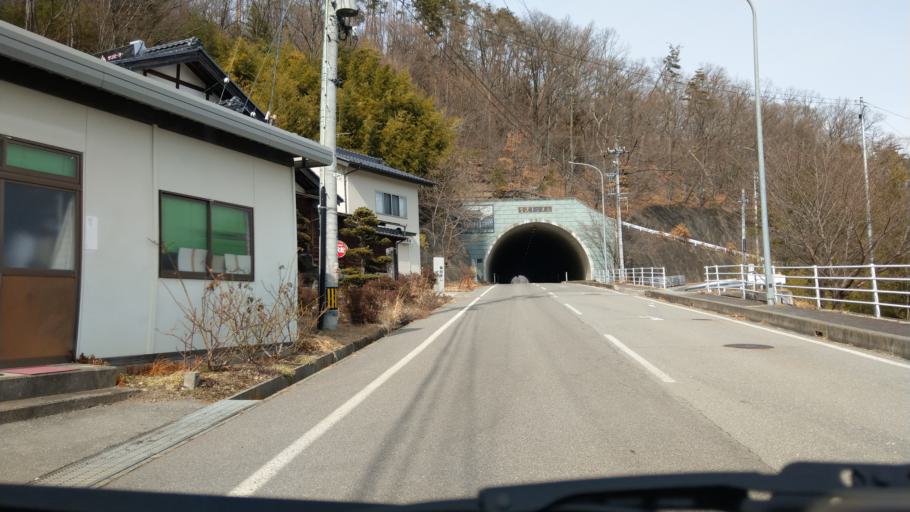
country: JP
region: Nagano
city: Komoro
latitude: 36.2948
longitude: 138.4193
